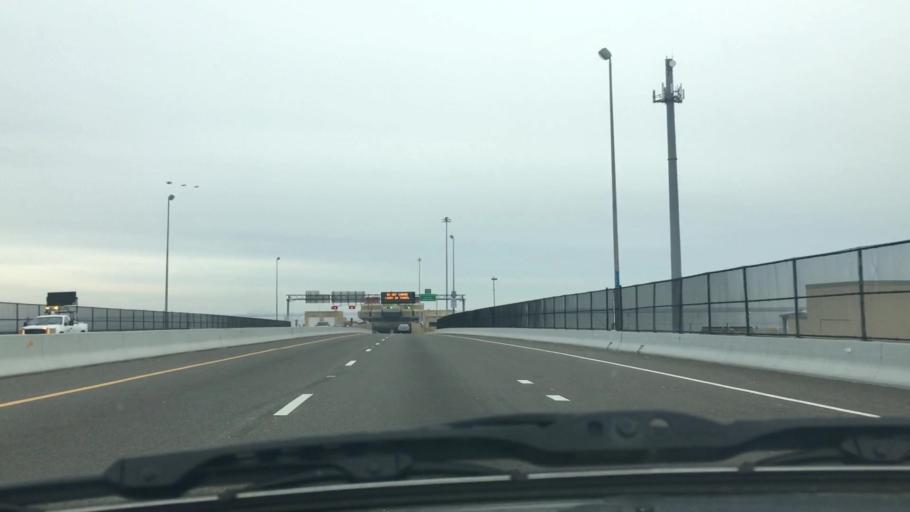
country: US
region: Virginia
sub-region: City of Newport News
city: Newport News
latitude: 36.9639
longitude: -76.4129
